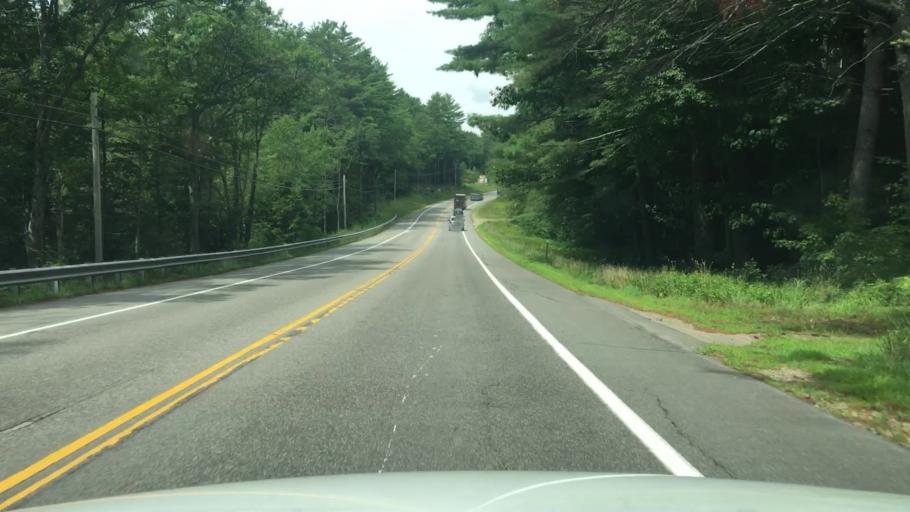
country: US
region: New Hampshire
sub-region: Grafton County
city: Ashland
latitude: 43.6230
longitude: -71.6102
